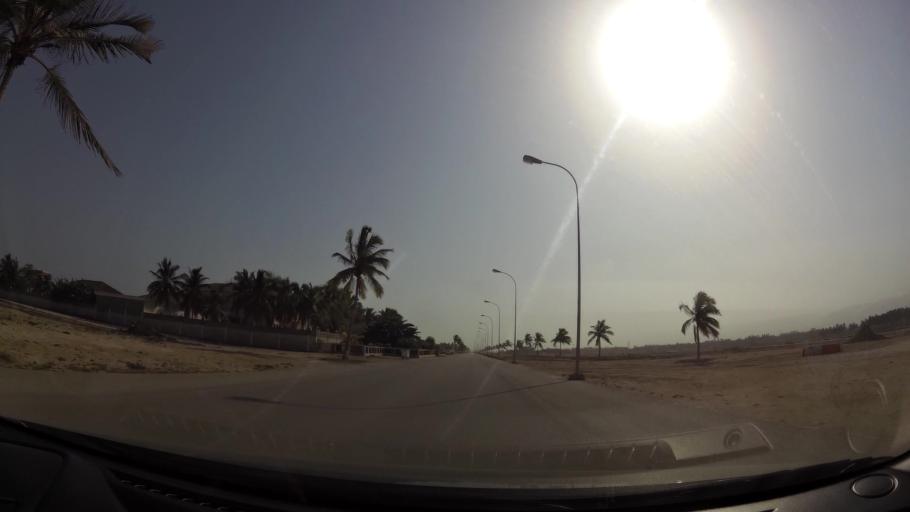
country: OM
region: Zufar
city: Salalah
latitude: 16.9948
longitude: 54.0572
